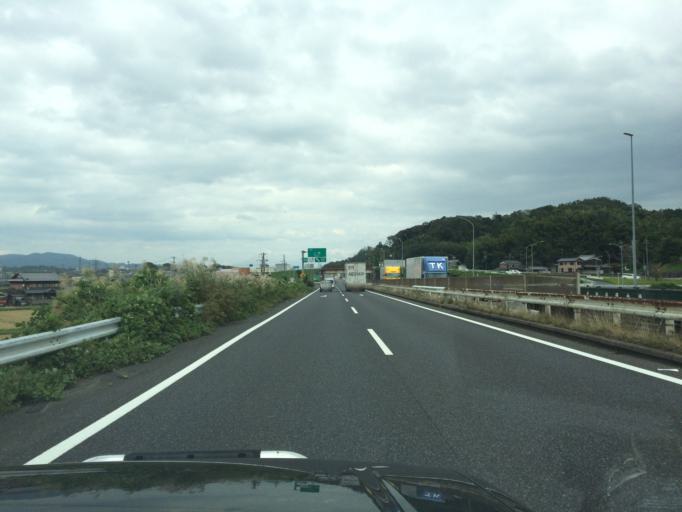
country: JP
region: Mie
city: Ueno-ebisumachi
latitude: 34.7463
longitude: 136.1203
